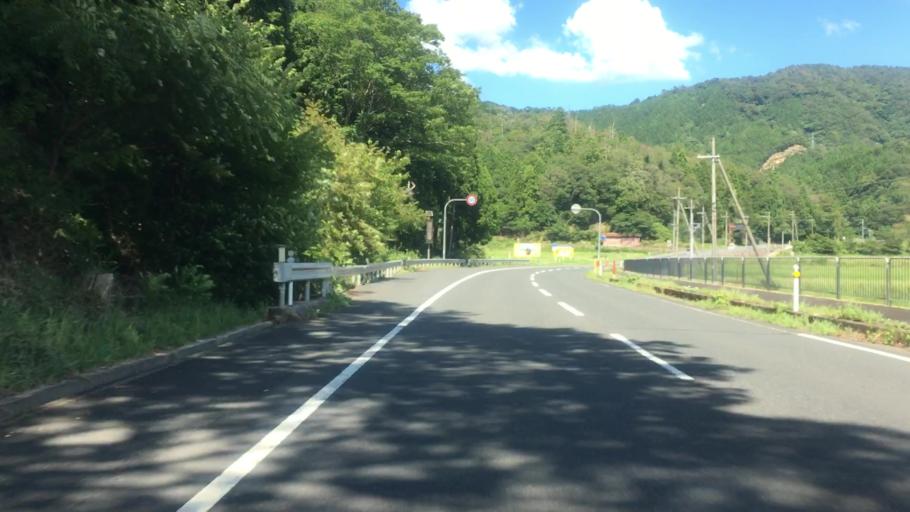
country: JP
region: Hyogo
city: Toyooka
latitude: 35.5751
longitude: 134.9858
